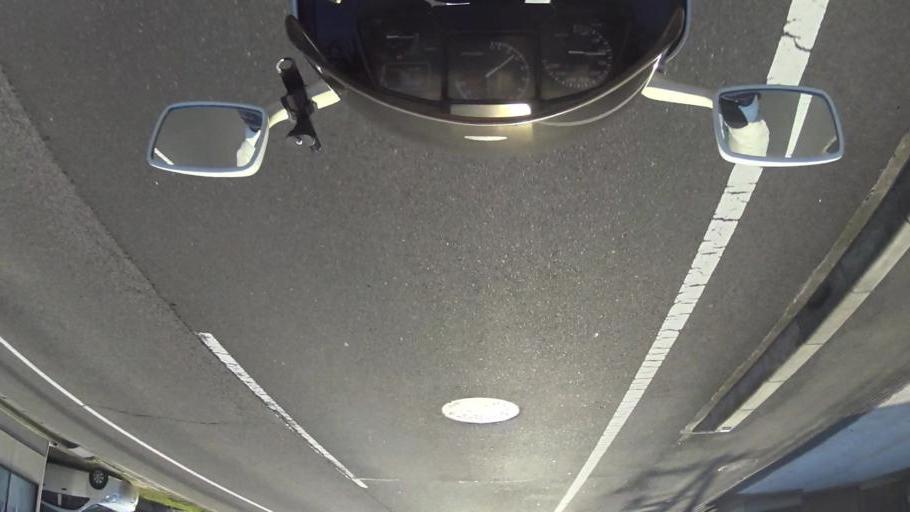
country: JP
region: Hyogo
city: Toyooka
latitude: 35.6019
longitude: 134.8946
